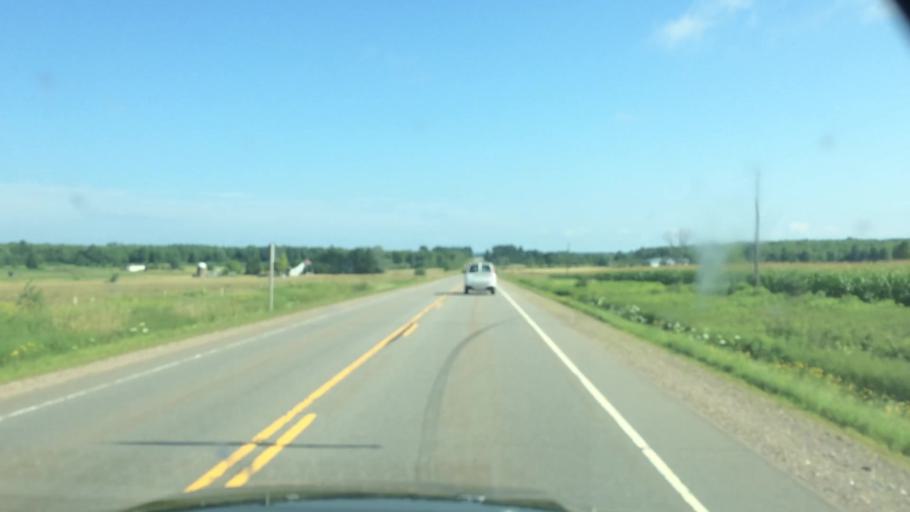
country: US
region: Wisconsin
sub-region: Lincoln County
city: Merrill
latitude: 45.1532
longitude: -89.4667
